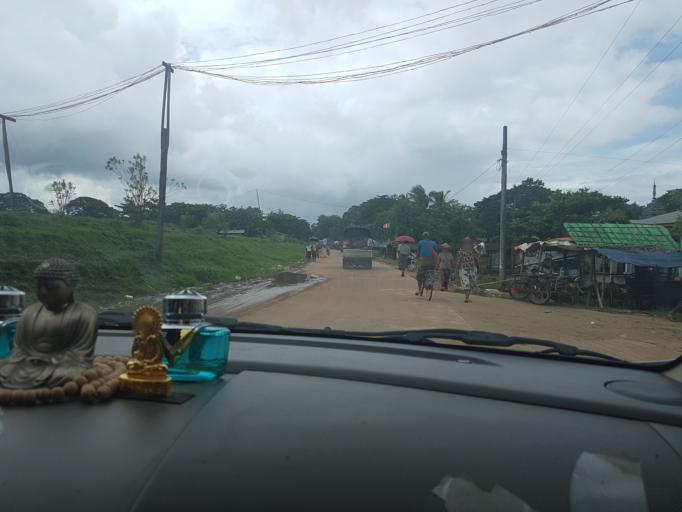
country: MM
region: Bago
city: Nyaunglebin
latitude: 17.9141
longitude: 96.8437
